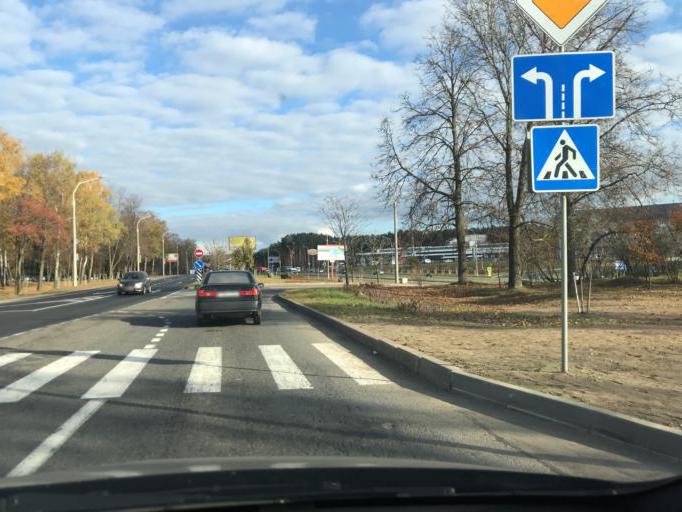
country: BY
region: Minsk
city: Borovlyany
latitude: 53.9615
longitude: 27.6288
